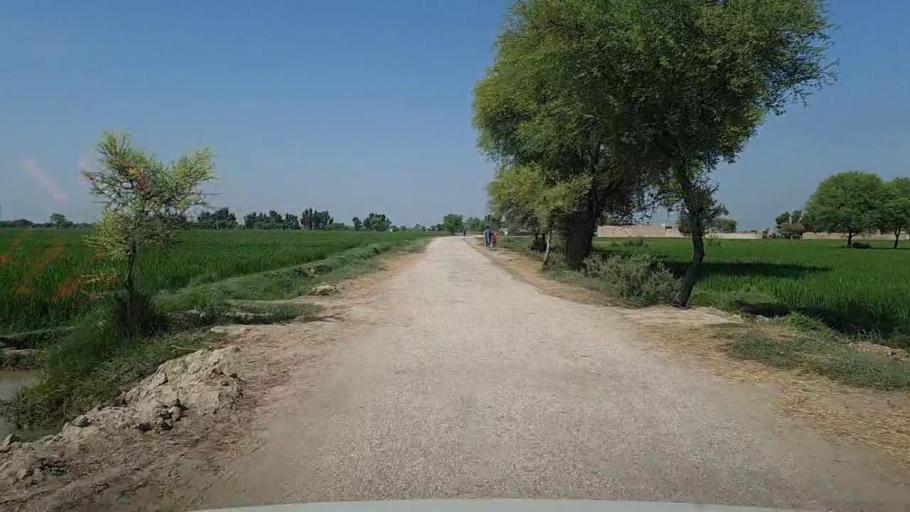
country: PK
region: Sindh
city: Kandhkot
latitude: 28.3276
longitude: 69.3670
